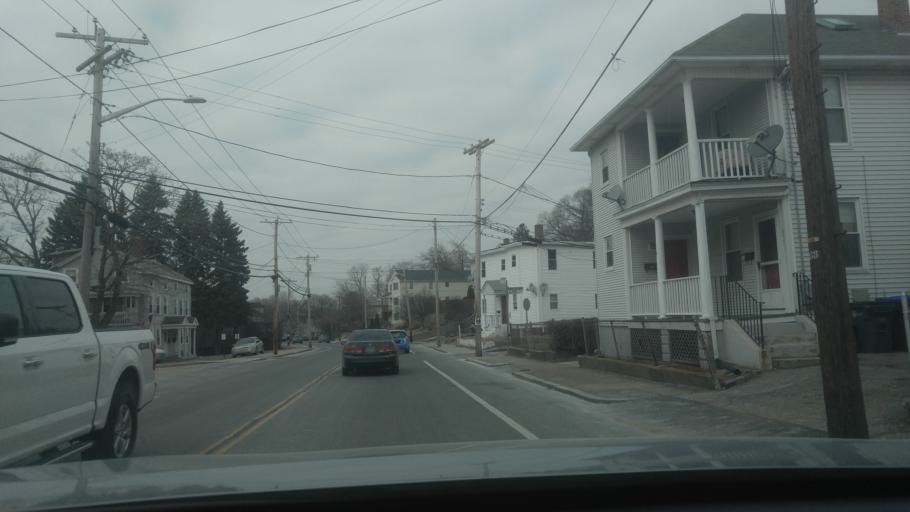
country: US
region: Rhode Island
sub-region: Providence County
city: North Providence
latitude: 41.8283
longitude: -71.4617
